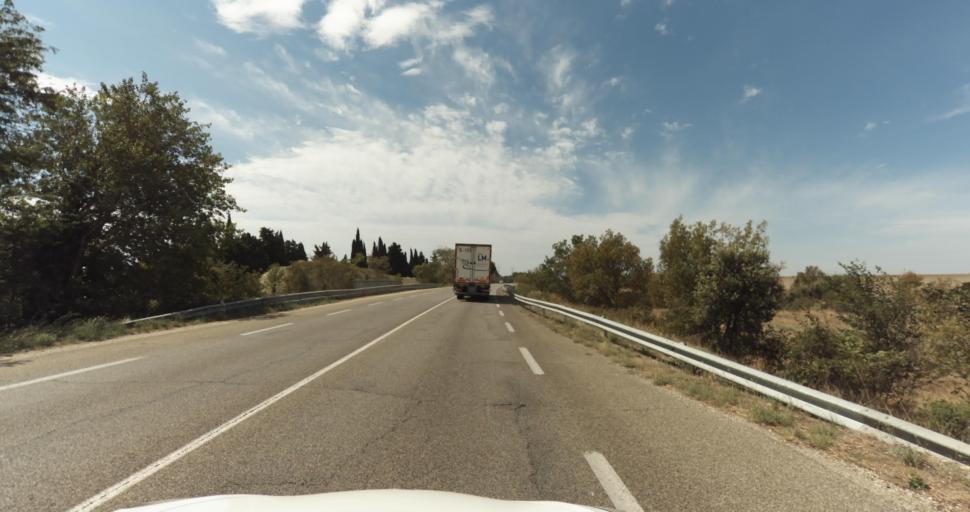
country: FR
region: Provence-Alpes-Cote d'Azur
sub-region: Departement des Bouches-du-Rhone
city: Miramas
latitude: 43.5717
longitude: 4.9822
